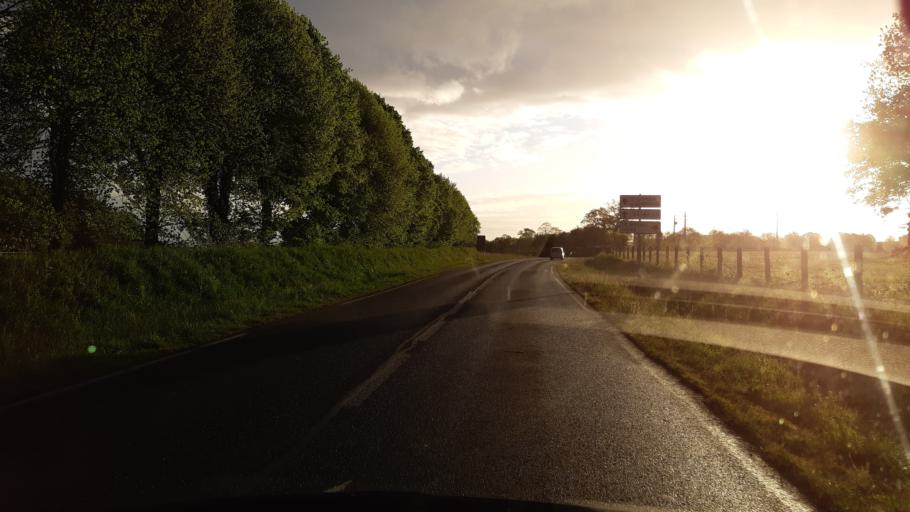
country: FR
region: Lower Normandy
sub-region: Departement de la Manche
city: Agneaux
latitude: 49.0303
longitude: -1.1392
